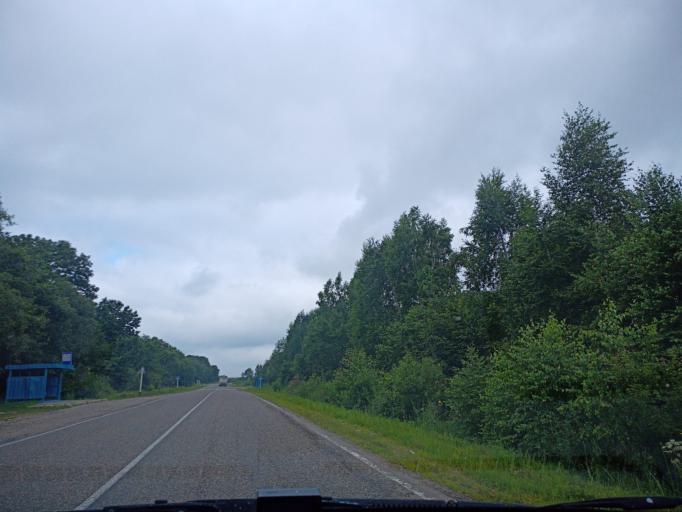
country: RU
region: Primorskiy
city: Novopokrovka
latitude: 45.9711
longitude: 134.2323
